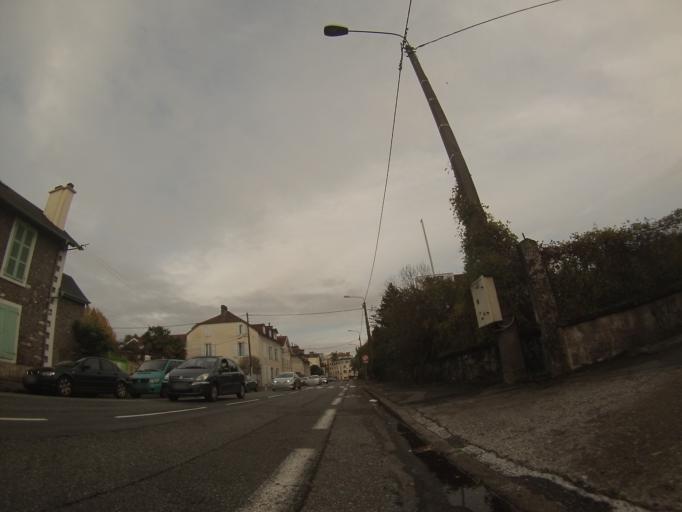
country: FR
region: Aquitaine
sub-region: Departement des Pyrenees-Atlantiques
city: Jurancon
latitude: 43.2860
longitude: -0.3825
